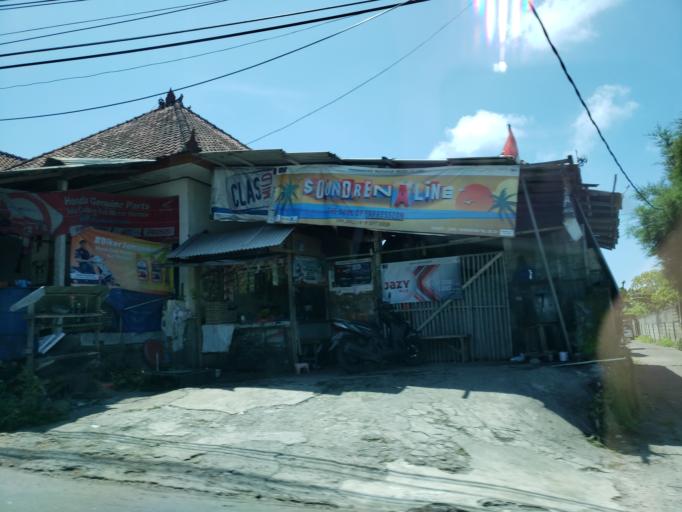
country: ID
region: Bali
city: Kangin
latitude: -8.8308
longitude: 115.1305
